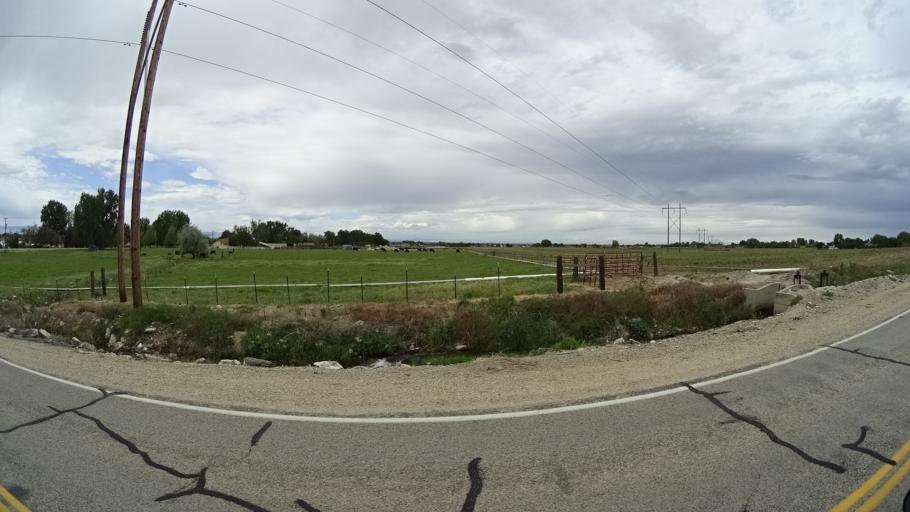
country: US
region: Idaho
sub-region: Ada County
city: Kuna
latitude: 43.5477
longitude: -116.4139
